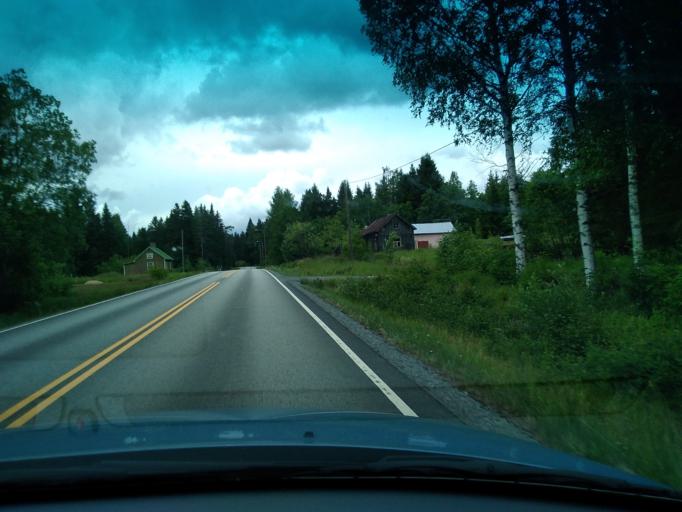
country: FI
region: Central Finland
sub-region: Saarijaervi-Viitasaari
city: Pylkoenmaeki
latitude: 62.6473
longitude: 24.9425
